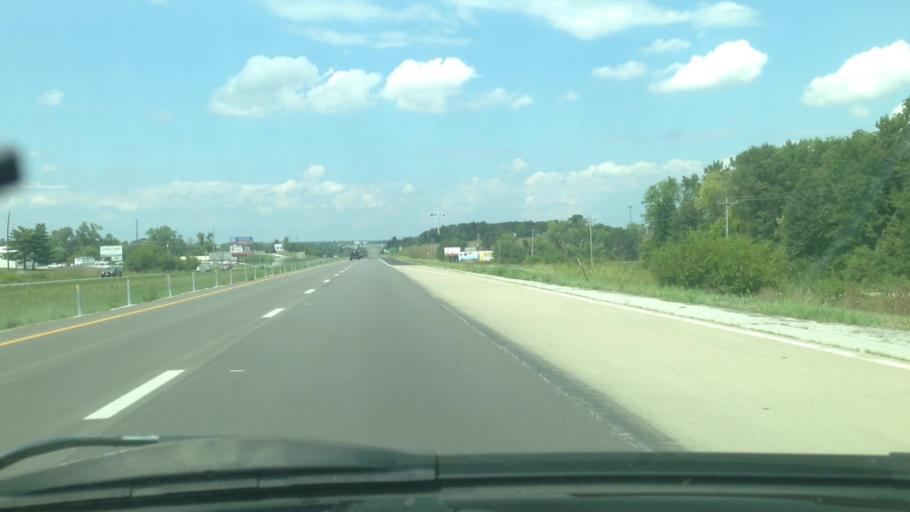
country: US
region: Missouri
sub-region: Lincoln County
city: Moscow Mills
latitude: 38.9124
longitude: -90.9237
